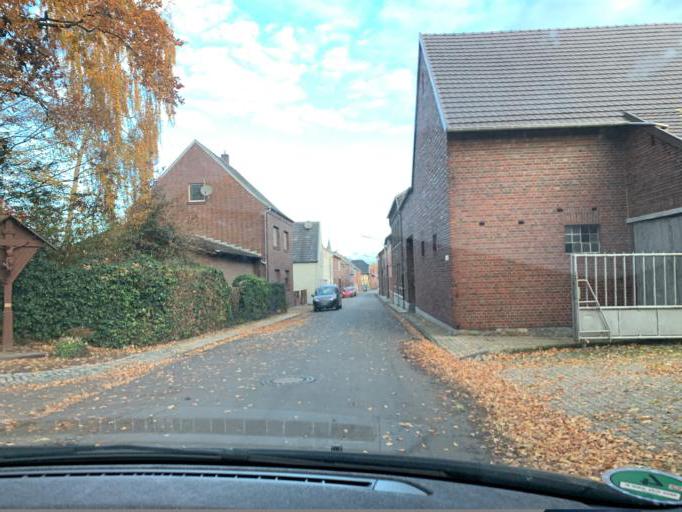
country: DE
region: North Rhine-Westphalia
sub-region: Regierungsbezirk Koln
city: Titz
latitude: 51.0429
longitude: 6.4065
